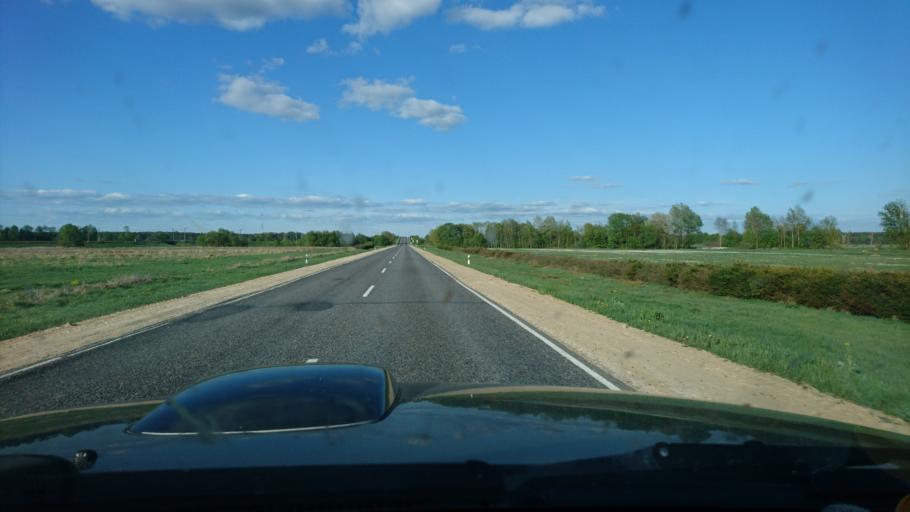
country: BY
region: Brest
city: Nyakhachava
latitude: 52.6346
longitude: 25.1867
